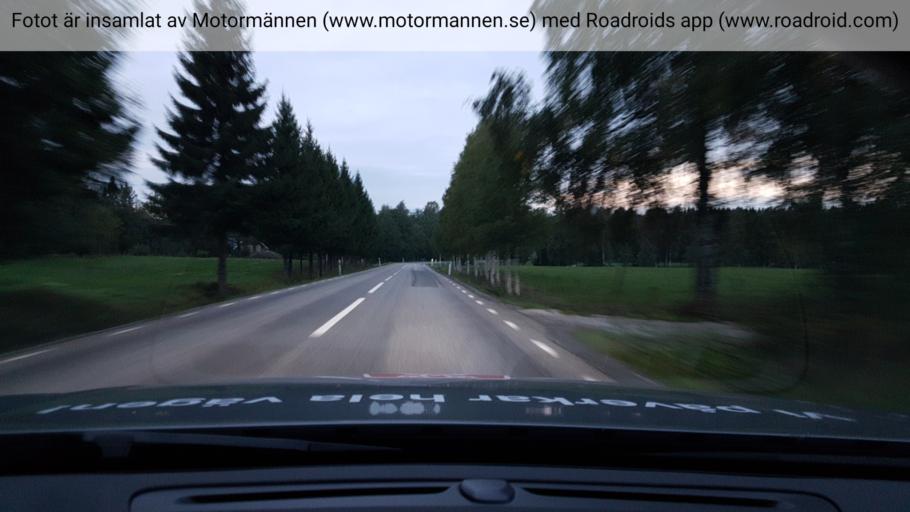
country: SE
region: OErebro
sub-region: Nora Kommun
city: As
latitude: 59.4589
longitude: 14.8707
